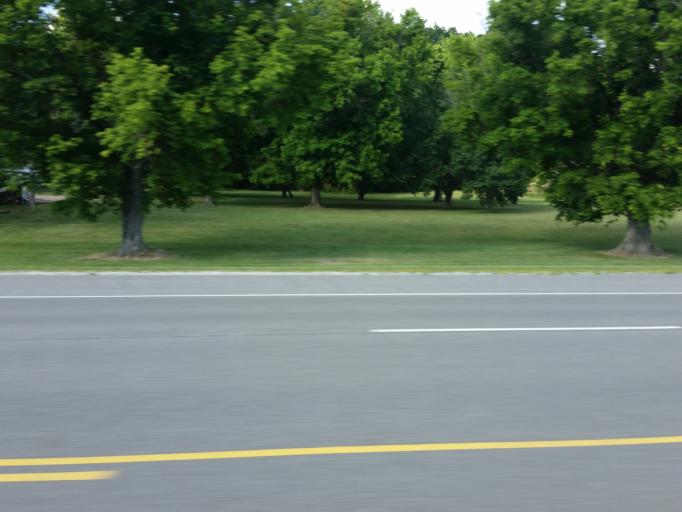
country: US
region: Tennessee
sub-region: Lewis County
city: Hohenwald
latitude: 35.5700
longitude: -87.4244
